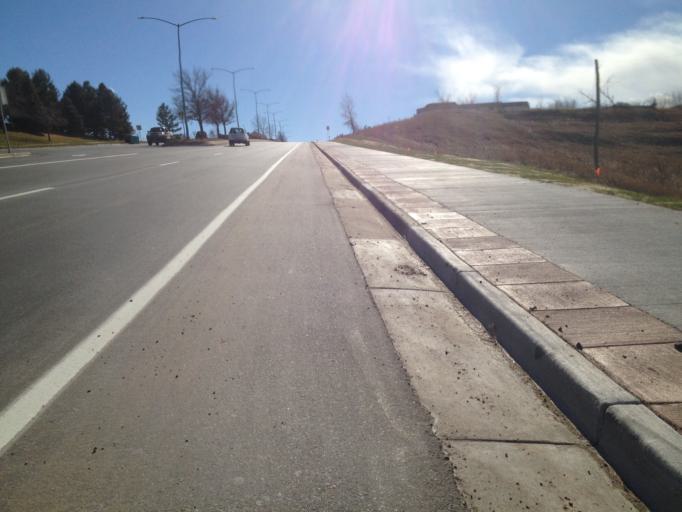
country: US
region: Colorado
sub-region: Boulder County
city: Superior
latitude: 39.9494
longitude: -105.1648
